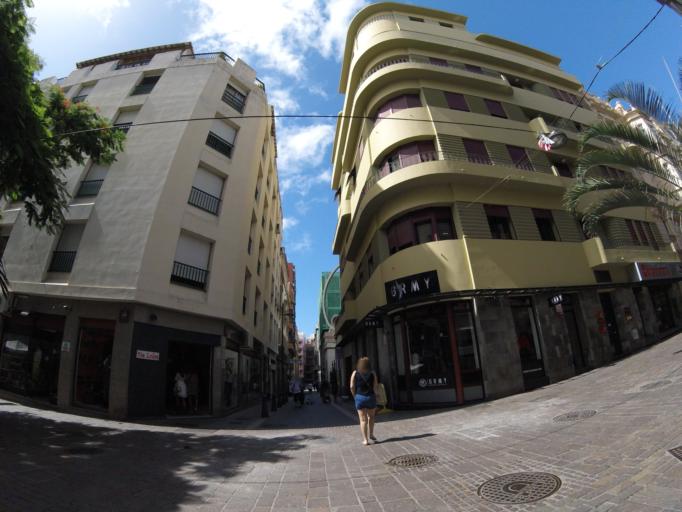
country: ES
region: Canary Islands
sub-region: Provincia de Santa Cruz de Tenerife
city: Santa Cruz de Tenerife
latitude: 28.4679
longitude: -16.2516
